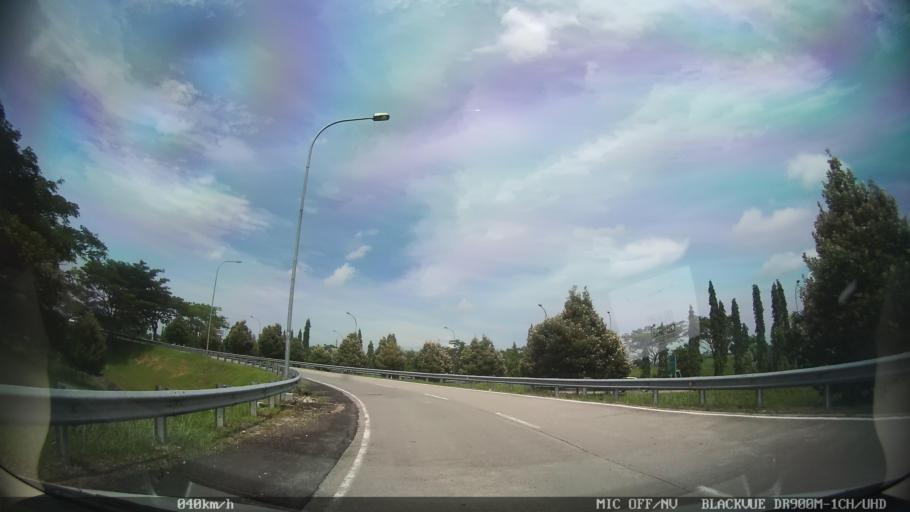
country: ID
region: North Sumatra
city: Percut
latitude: 3.6343
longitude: 98.8764
